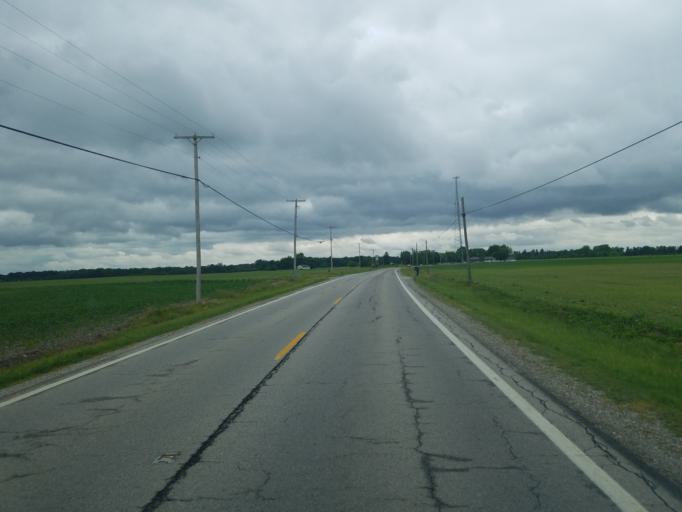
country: US
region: Ohio
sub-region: Marion County
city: Marion
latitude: 40.6292
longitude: -83.1390
